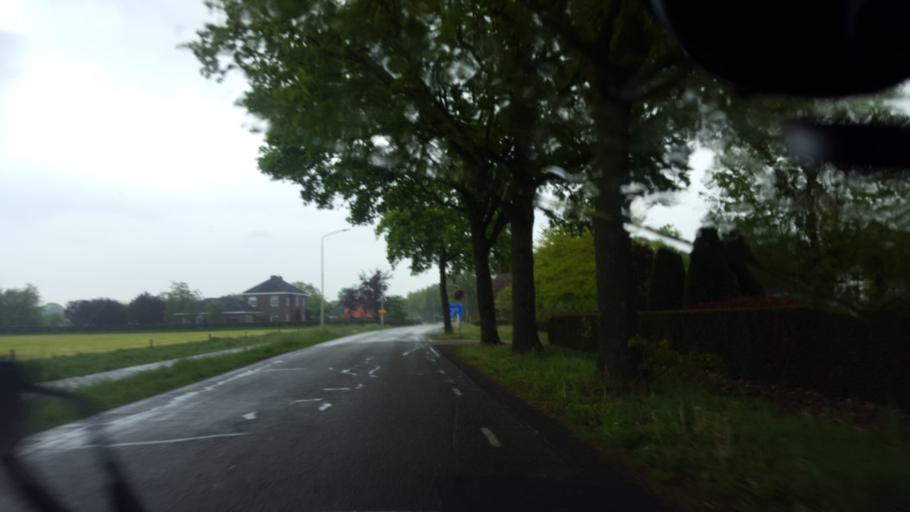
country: NL
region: North Brabant
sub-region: Gemeente Someren
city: Someren
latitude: 51.3920
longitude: 5.6972
